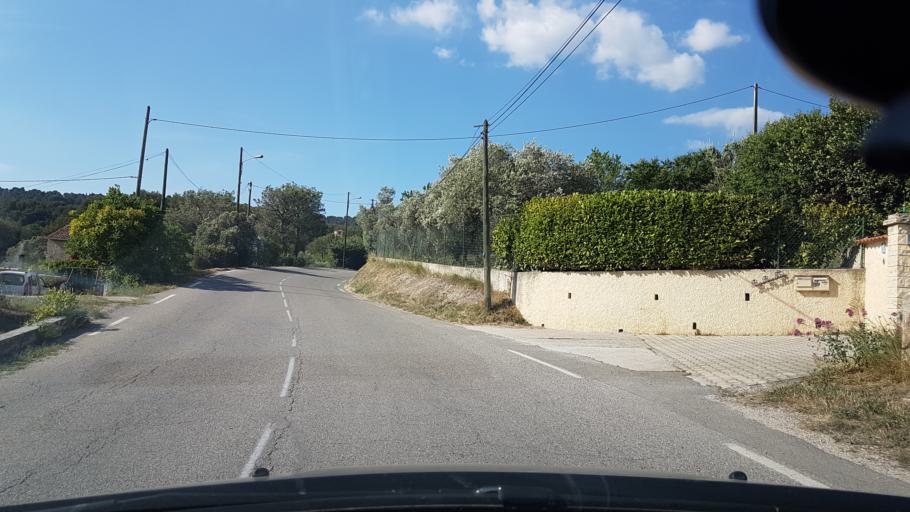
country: FR
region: Provence-Alpes-Cote d'Azur
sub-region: Departement des Bouches-du-Rhone
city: Carnoux-en-Provence
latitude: 43.2388
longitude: 5.5620
